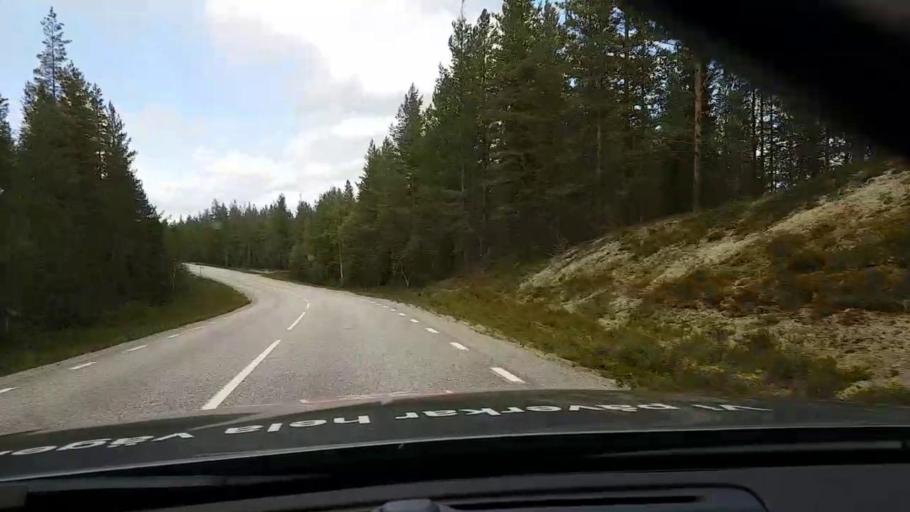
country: SE
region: Vaesternorrland
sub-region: OErnskoeldsviks Kommun
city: Bredbyn
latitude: 63.7022
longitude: 17.7634
